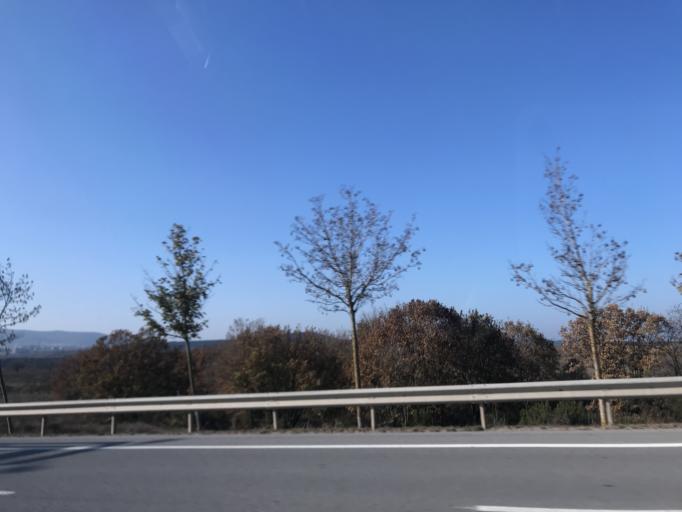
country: TR
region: Kocaeli
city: Balcik
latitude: 40.9402
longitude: 29.3687
